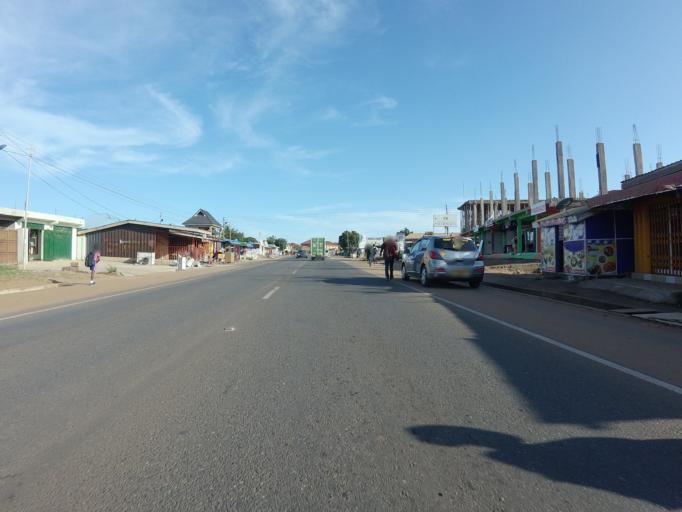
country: GH
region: Greater Accra
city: Nungua
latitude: 5.6353
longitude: -0.0912
